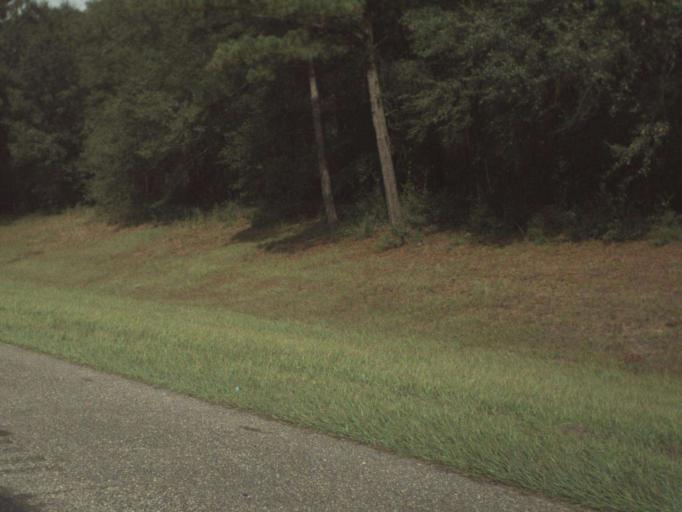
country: US
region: Florida
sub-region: Gadsden County
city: Gretna
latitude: 30.5595
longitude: -84.6405
